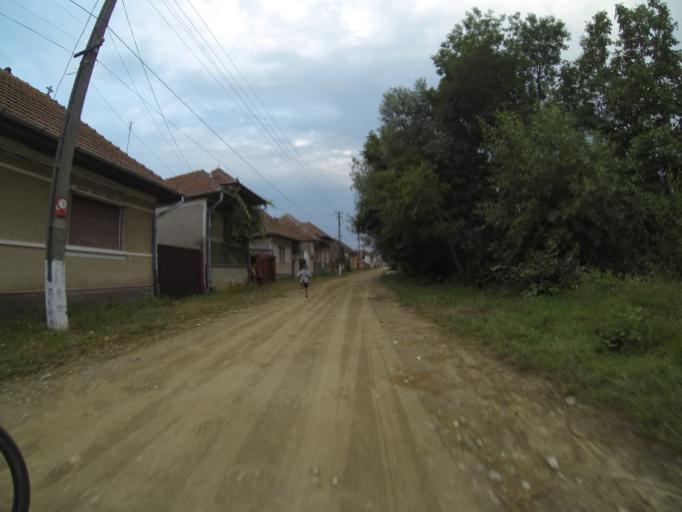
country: RO
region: Brasov
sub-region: Comuna Sinca Veche
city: Sinca Veche
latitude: 45.7656
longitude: 25.1733
